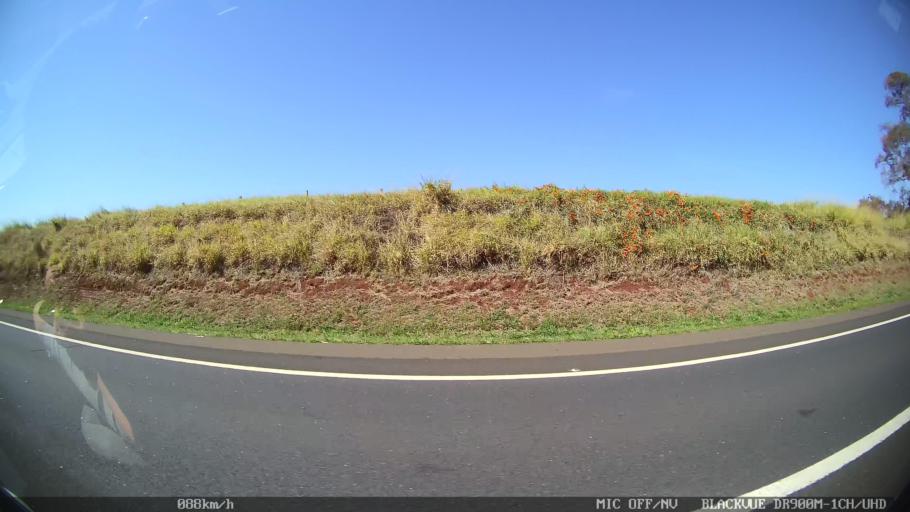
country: BR
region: Sao Paulo
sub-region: Batatais
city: Batatais
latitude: -20.7931
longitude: -47.5622
